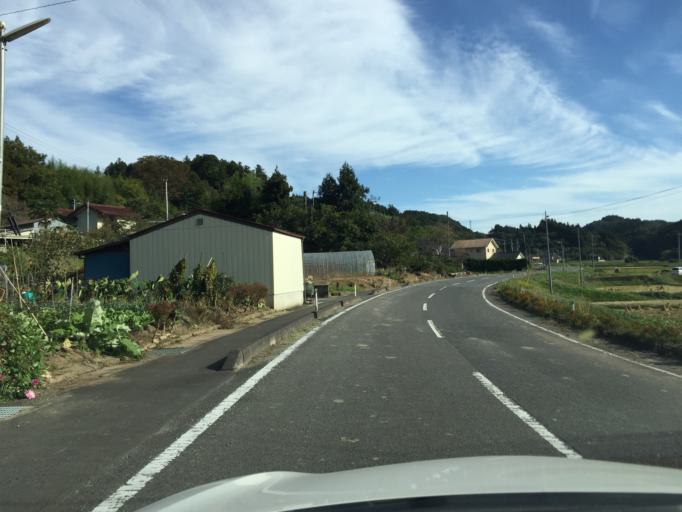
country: JP
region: Fukushima
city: Miharu
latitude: 37.3360
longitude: 140.4872
